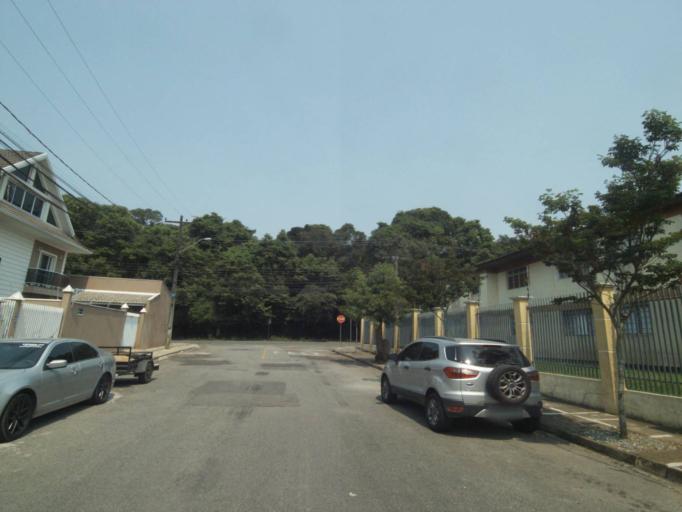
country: BR
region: Parana
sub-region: Sao Jose Dos Pinhais
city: Sao Jose dos Pinhais
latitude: -25.5233
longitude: -49.2389
